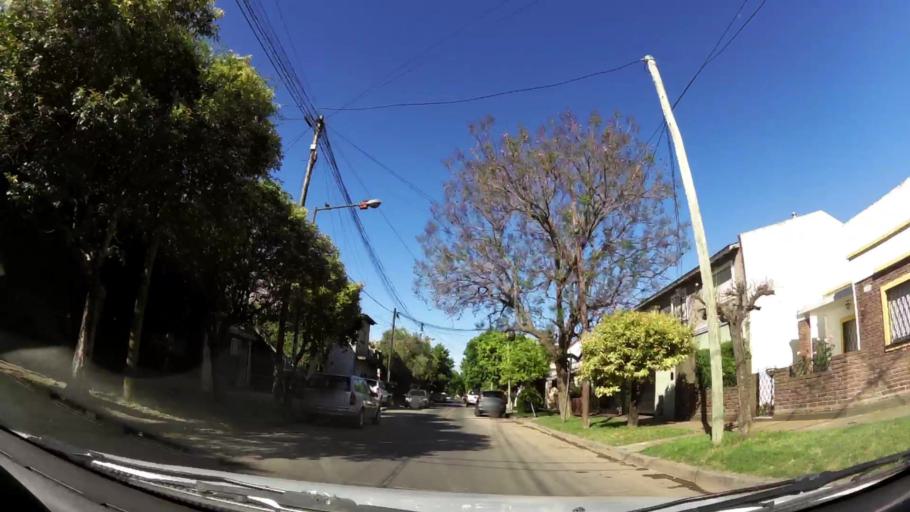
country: AR
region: Buenos Aires
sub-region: Partido de San Isidro
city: San Isidro
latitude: -34.4789
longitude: -58.5404
